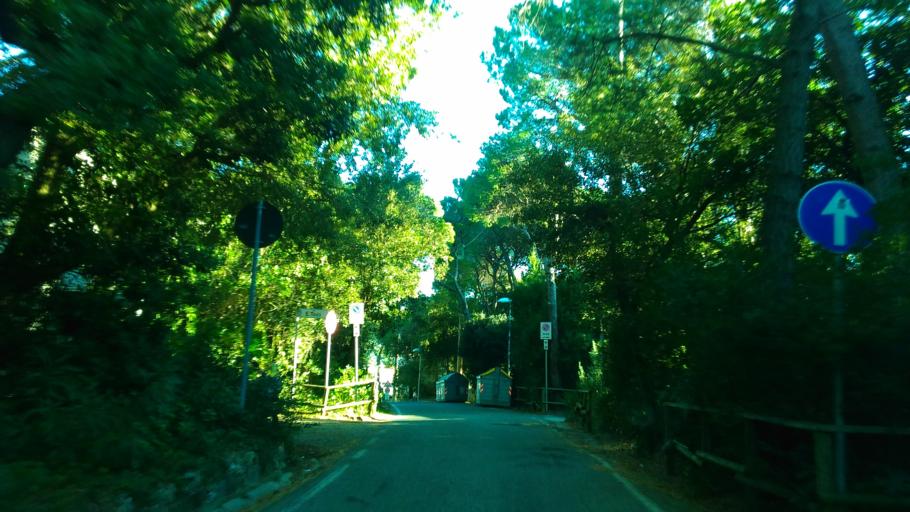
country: IT
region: Tuscany
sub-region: Provincia di Livorno
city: Quercianella
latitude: 43.4599
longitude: 10.3628
